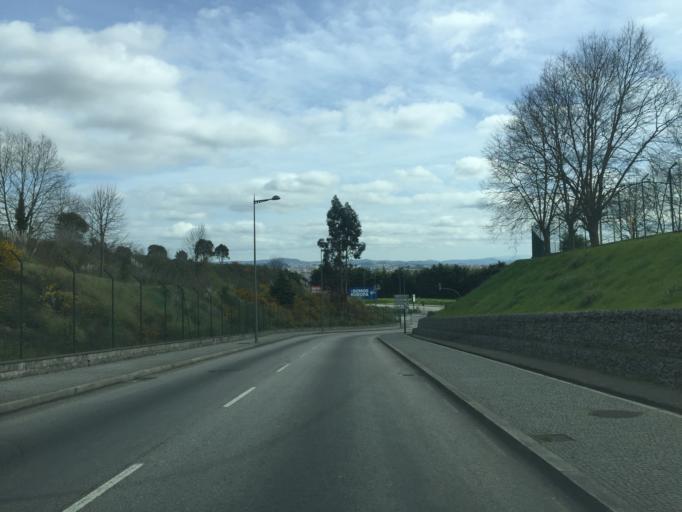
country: PT
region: Porto
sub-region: Porto
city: Porto
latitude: 41.1375
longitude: -8.6029
